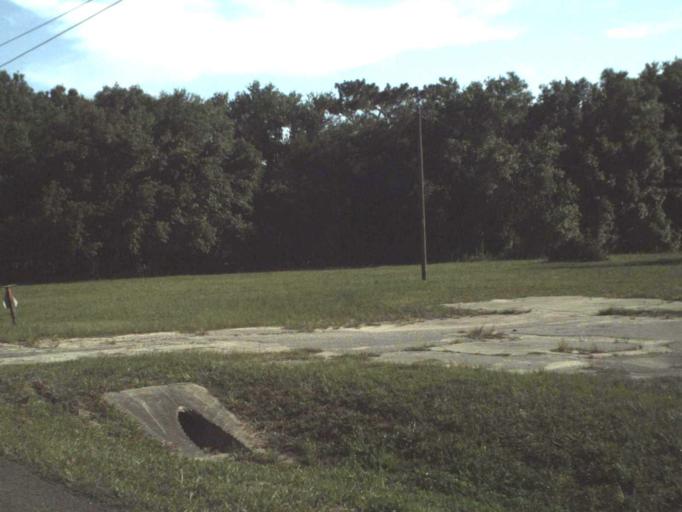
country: US
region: Florida
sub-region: Lake County
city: Clermont
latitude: 28.3824
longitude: -81.8243
